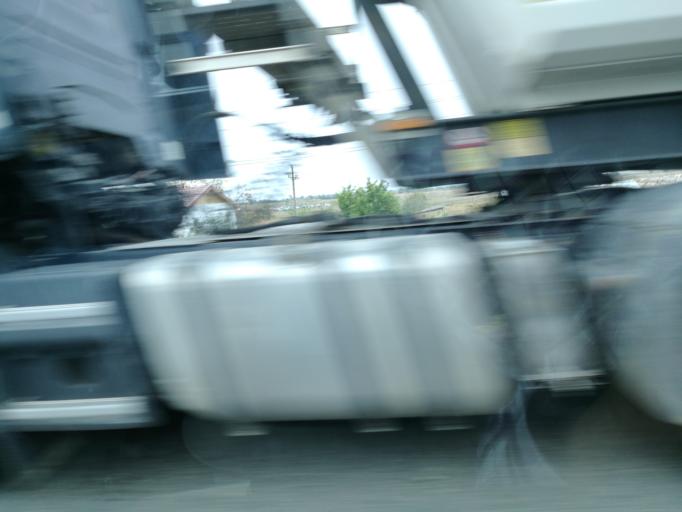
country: RO
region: Braila
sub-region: Municipiul Braila
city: Braila
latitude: 45.2845
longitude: 28.0077
